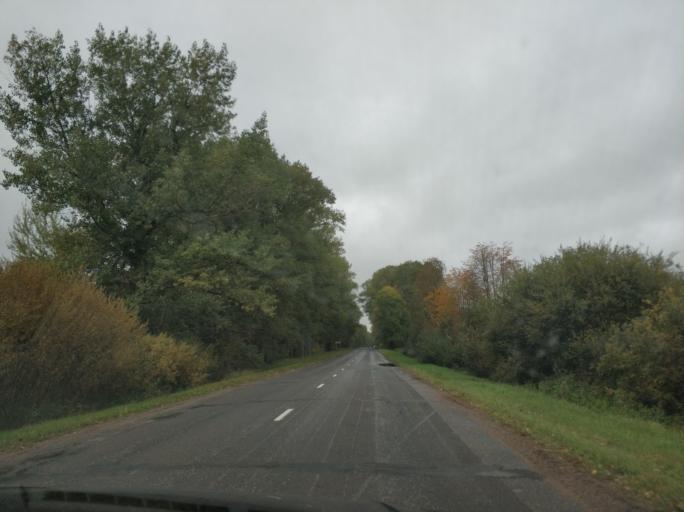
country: BY
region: Vitebsk
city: Polatsk
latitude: 55.4315
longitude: 28.9926
